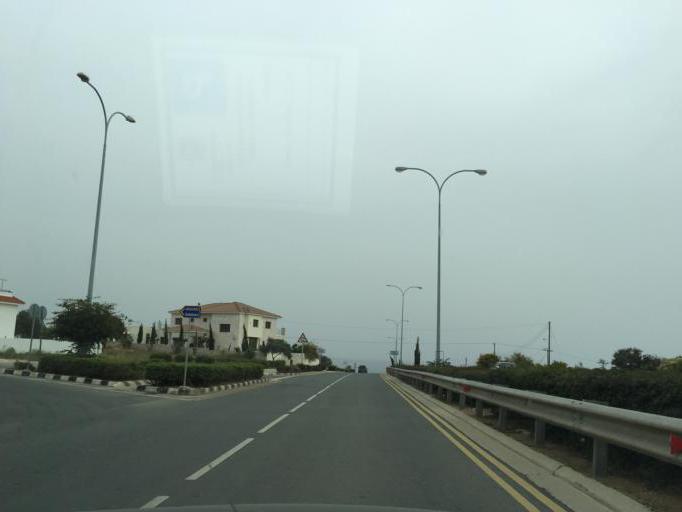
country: CY
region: Ammochostos
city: Ayia Napa
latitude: 35.0003
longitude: 33.9998
